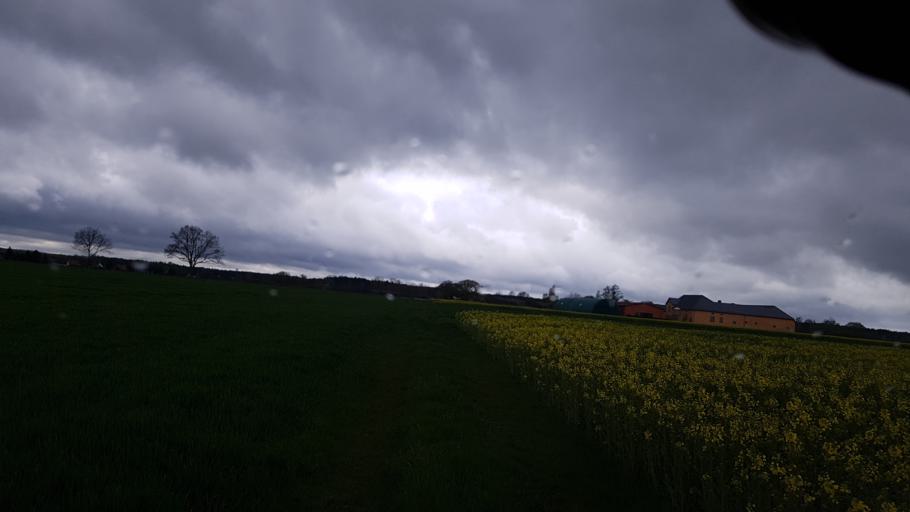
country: DE
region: Brandenburg
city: Doberlug-Kirchhain
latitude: 51.6595
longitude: 13.5286
